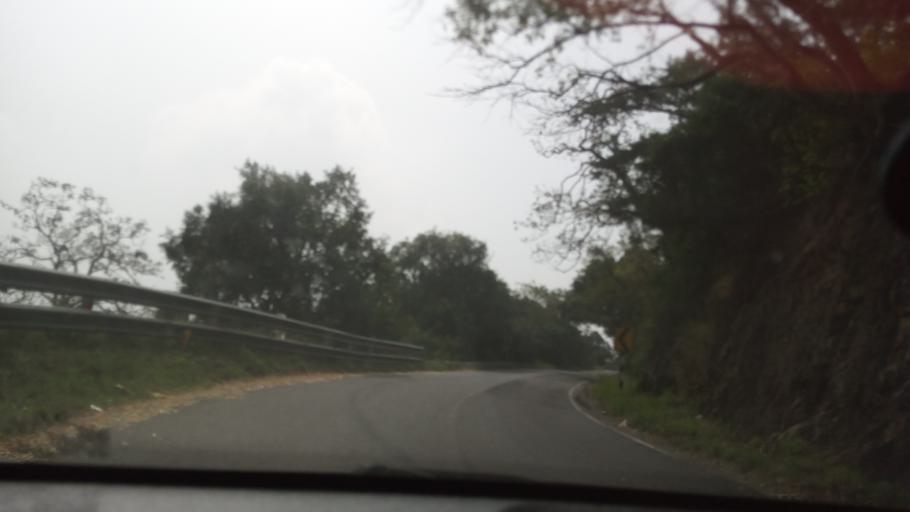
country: IN
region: Tamil Nadu
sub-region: Erode
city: Sathyamangalam
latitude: 11.5966
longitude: 77.1255
